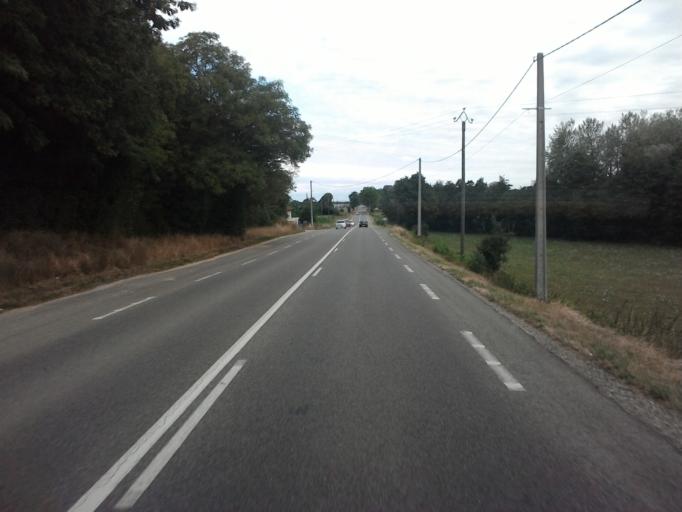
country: FR
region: Rhone-Alpes
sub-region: Departement de l'Ain
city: Saint-Martin-du-Mont
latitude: 46.0838
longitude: 5.3182
